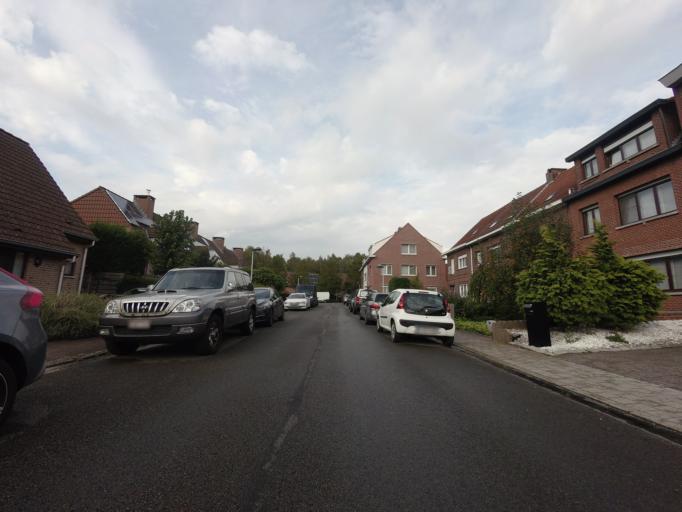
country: BE
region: Flanders
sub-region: Provincie Antwerpen
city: Rumst
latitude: 51.0805
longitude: 4.3996
